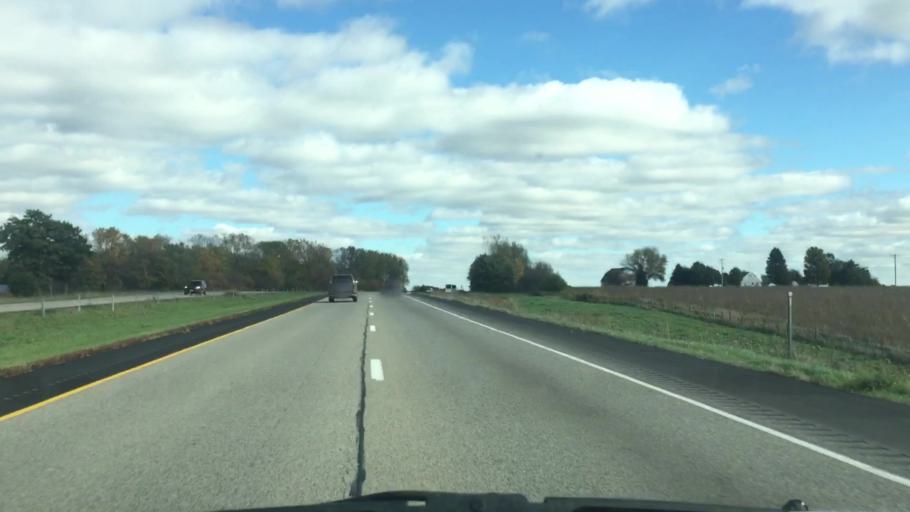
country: US
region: Iowa
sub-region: Muscatine County
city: West Liberty
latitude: 41.6574
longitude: -91.1985
